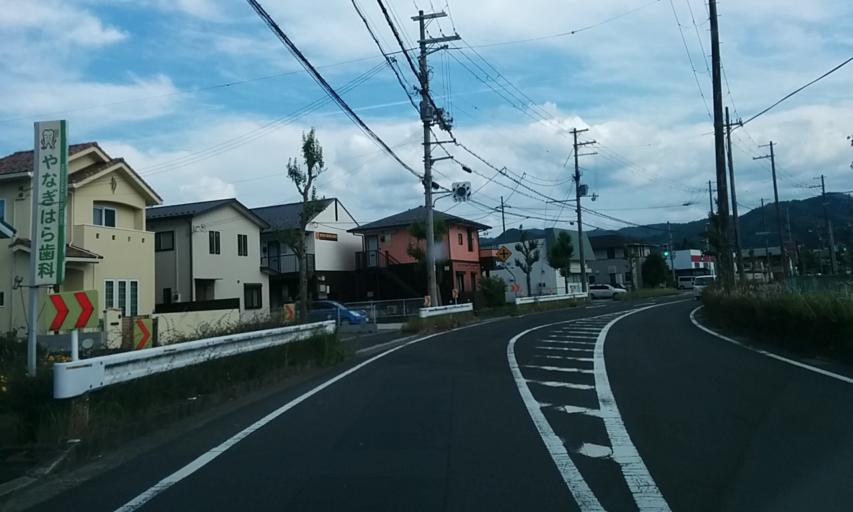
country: JP
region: Kyoto
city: Ayabe
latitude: 35.3064
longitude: 135.2622
